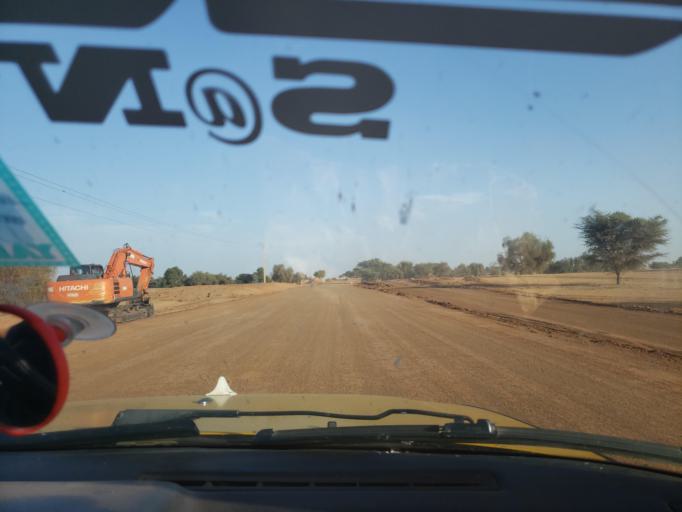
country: SN
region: Louga
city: Dara
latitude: 15.4169
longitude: -15.7146
